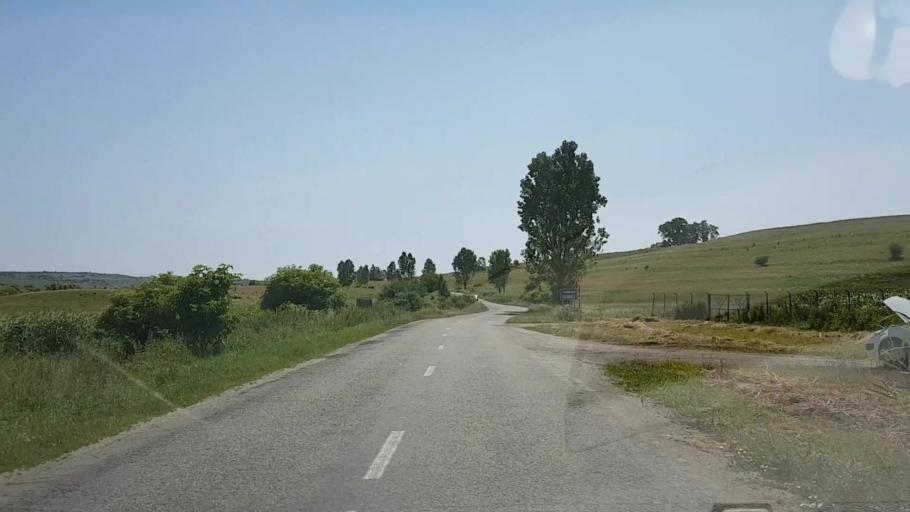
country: RO
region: Sibiu
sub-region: Comuna Merghindeal
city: Merghindeal
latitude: 45.9573
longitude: 24.7638
